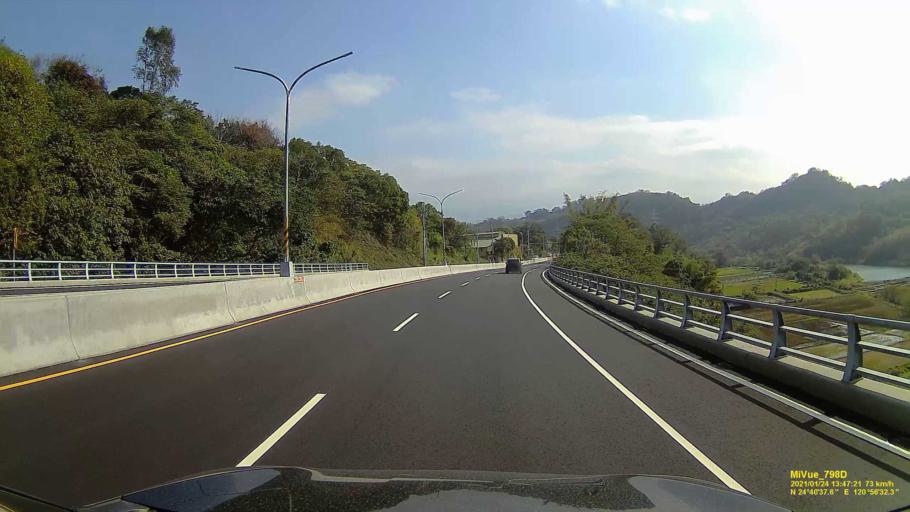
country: TW
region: Taiwan
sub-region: Hsinchu
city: Hsinchu
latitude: 24.6769
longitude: 120.9425
